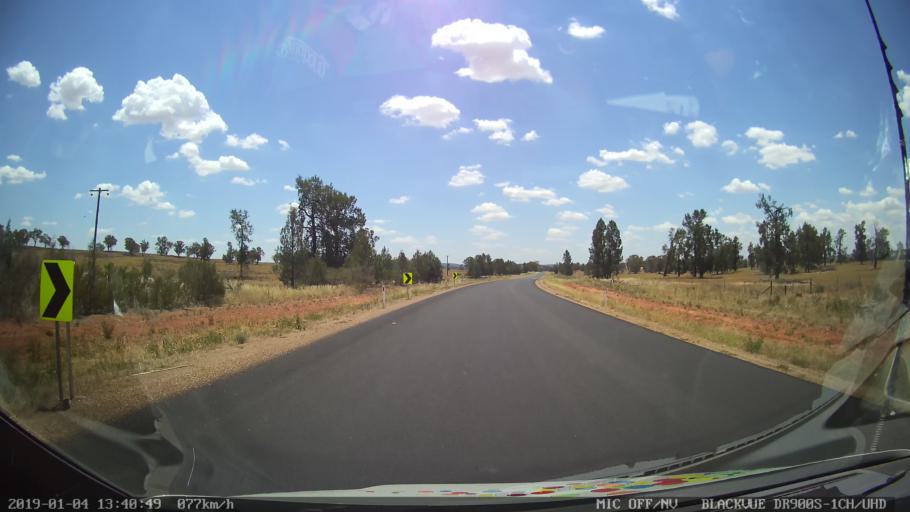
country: AU
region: New South Wales
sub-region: Dubbo Municipality
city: Dubbo
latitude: -32.5100
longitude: 148.5543
